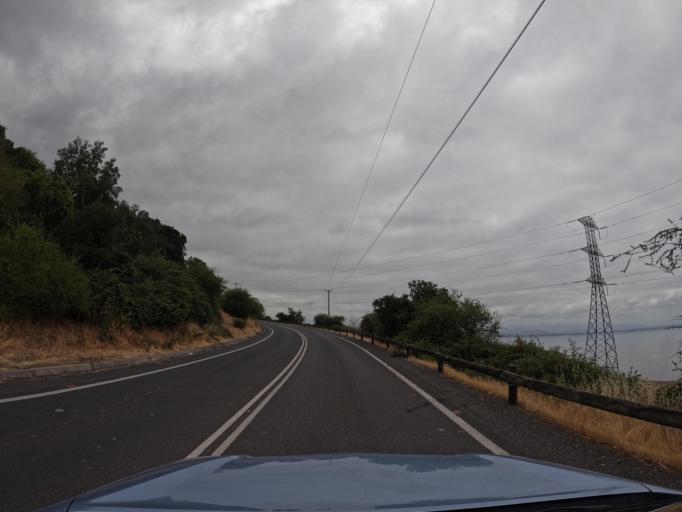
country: CL
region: O'Higgins
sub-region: Provincia de Colchagua
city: Chimbarongo
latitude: -34.7376
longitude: -71.1177
